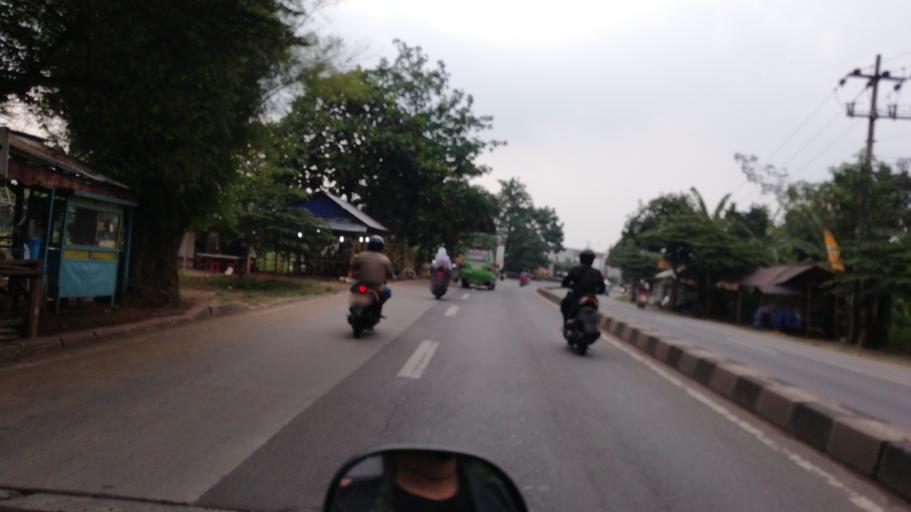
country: ID
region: West Java
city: Parung
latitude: -6.4898
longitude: 106.7377
